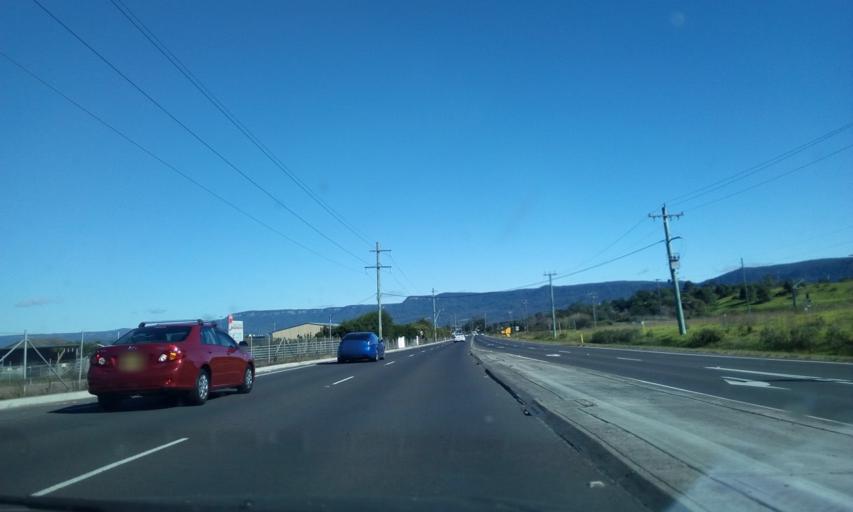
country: AU
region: New South Wales
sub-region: Wollongong
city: Berkeley
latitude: -34.4688
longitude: 150.8256
